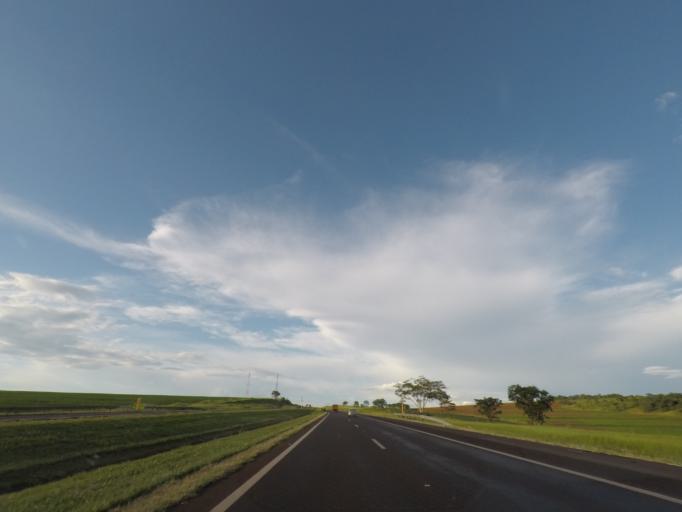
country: BR
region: Sao Paulo
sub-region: Ituverava
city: Ituverava
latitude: -20.2782
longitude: -47.7973
